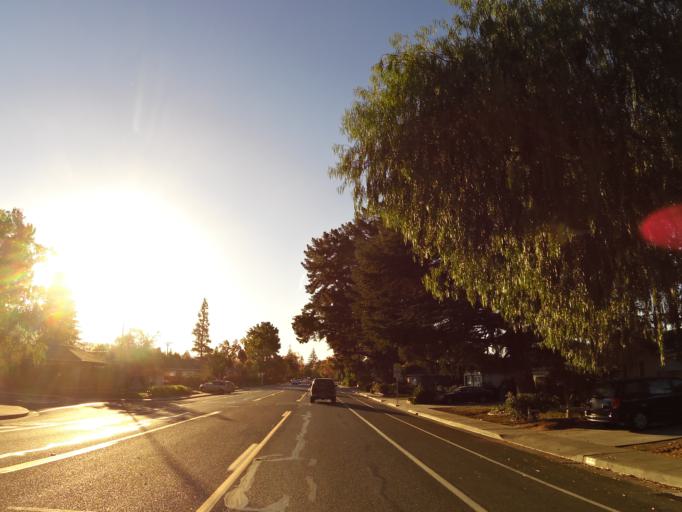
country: US
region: California
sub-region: Santa Clara County
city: Mountain View
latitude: 37.3734
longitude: -122.0902
